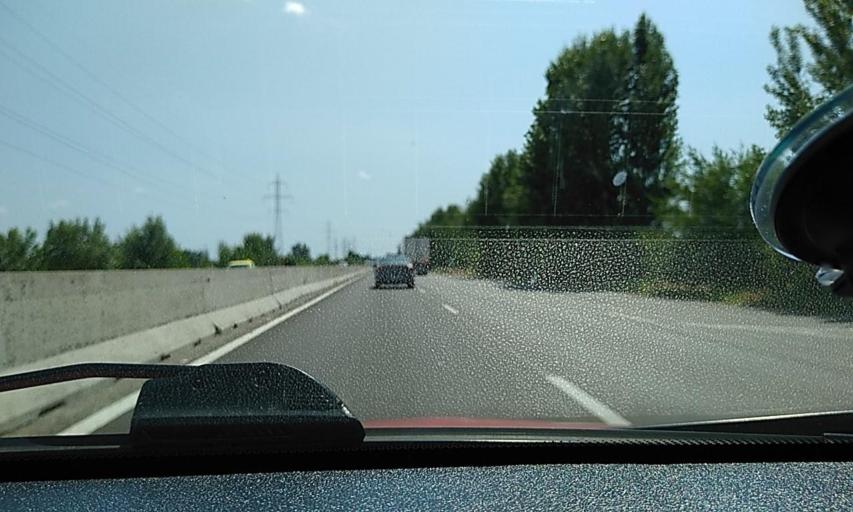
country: RO
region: Prahova
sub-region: Comuna Barcanesti
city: Tatarani
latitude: 44.8990
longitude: 26.0082
